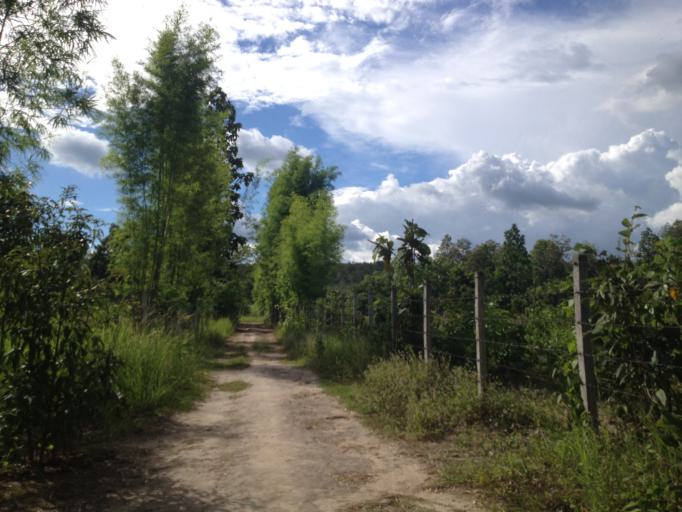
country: TH
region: Chiang Mai
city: Hang Dong
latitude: 18.7043
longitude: 98.8972
